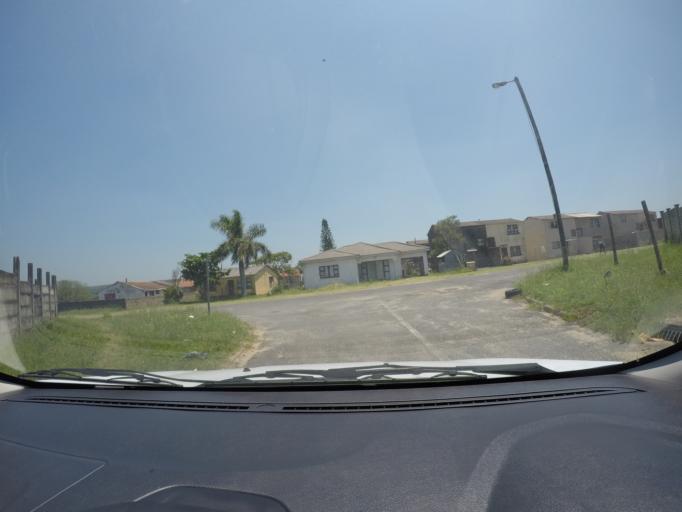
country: ZA
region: KwaZulu-Natal
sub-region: uThungulu District Municipality
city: eSikhawini
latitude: -28.8765
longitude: 31.9080
